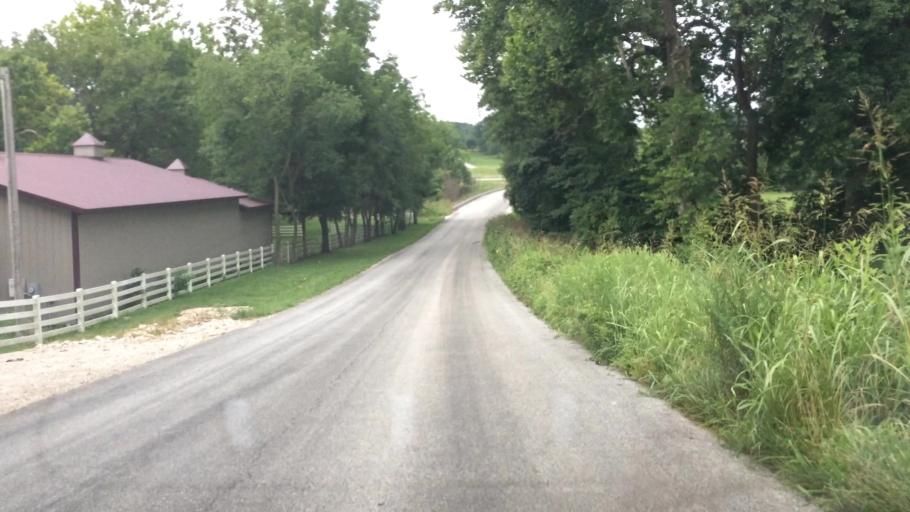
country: US
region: Missouri
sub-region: Webster County
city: Marshfield
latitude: 37.3058
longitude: -92.9846
